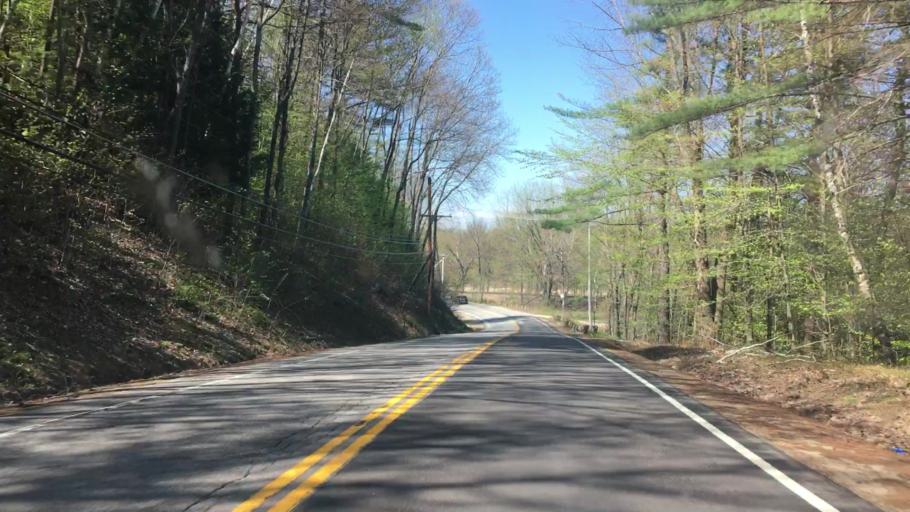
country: US
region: New Hampshire
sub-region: Grafton County
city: Plymouth
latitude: 43.7373
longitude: -71.6764
